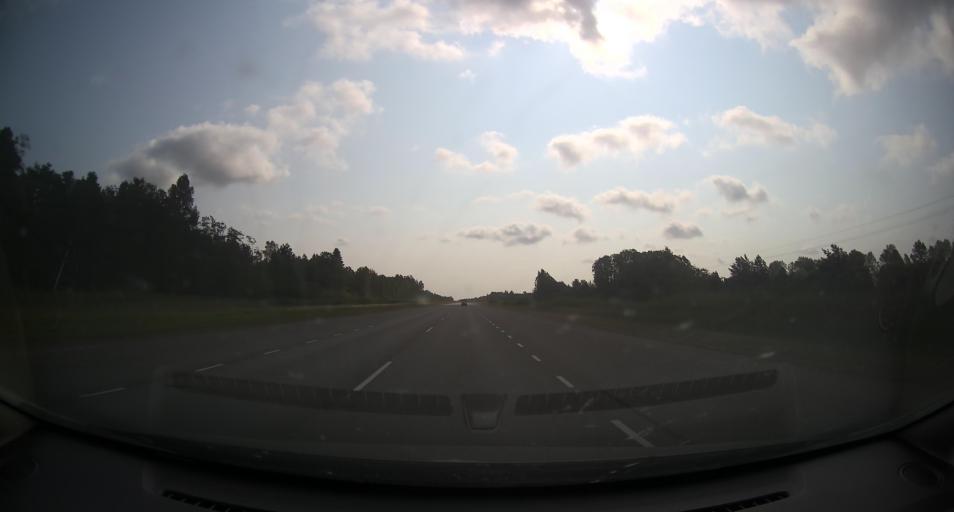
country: EE
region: Laeaene
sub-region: Lihula vald
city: Lihula
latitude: 58.5666
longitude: 23.7880
